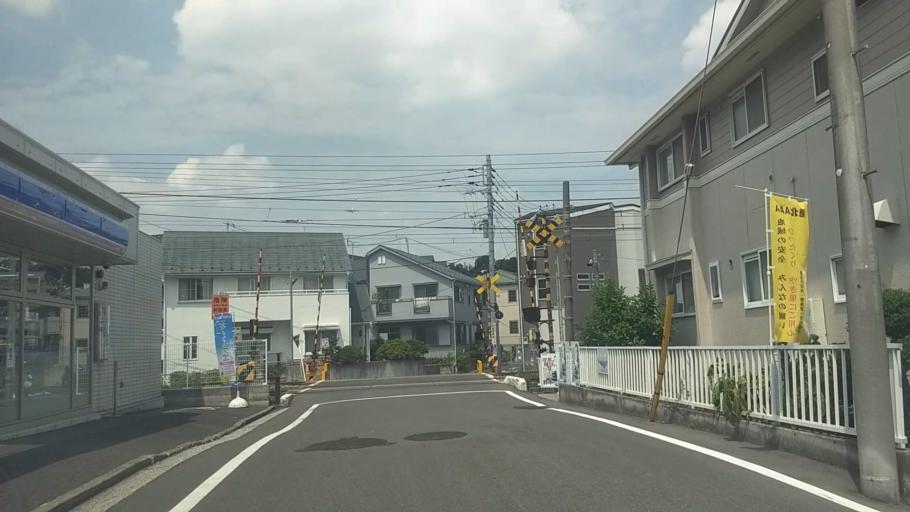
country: JP
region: Kanagawa
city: Yokohama
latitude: 35.5084
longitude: 139.6249
